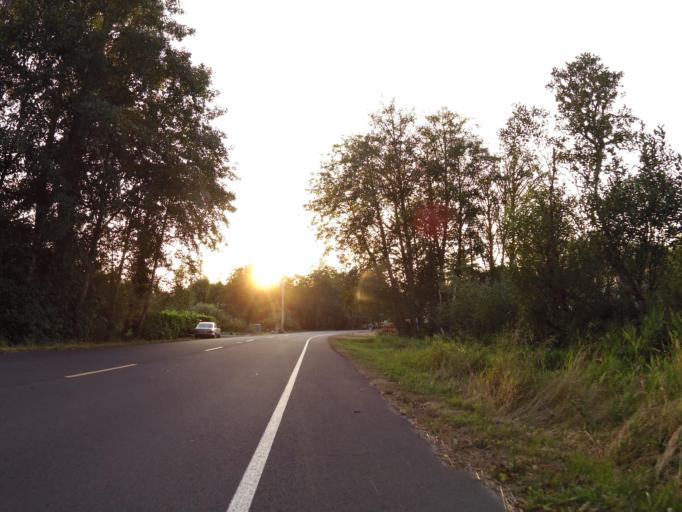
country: US
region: Oregon
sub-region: Clatsop County
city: Warrenton
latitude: 46.1579
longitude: -123.9419
